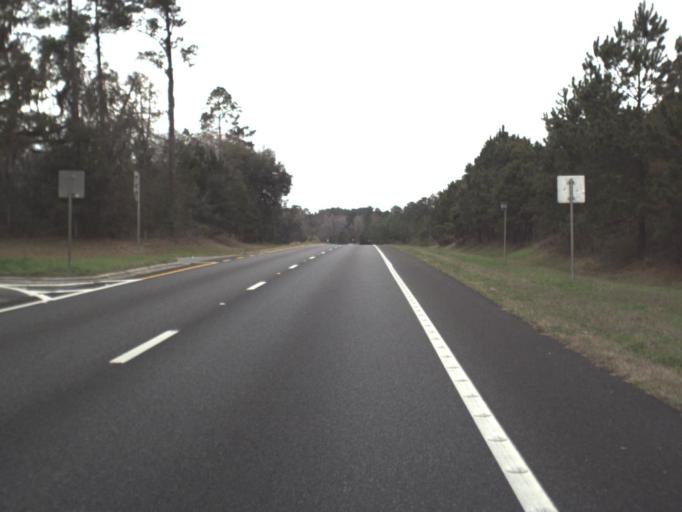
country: US
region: Florida
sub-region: Leon County
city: Tallahassee
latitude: 30.6424
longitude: -84.1684
